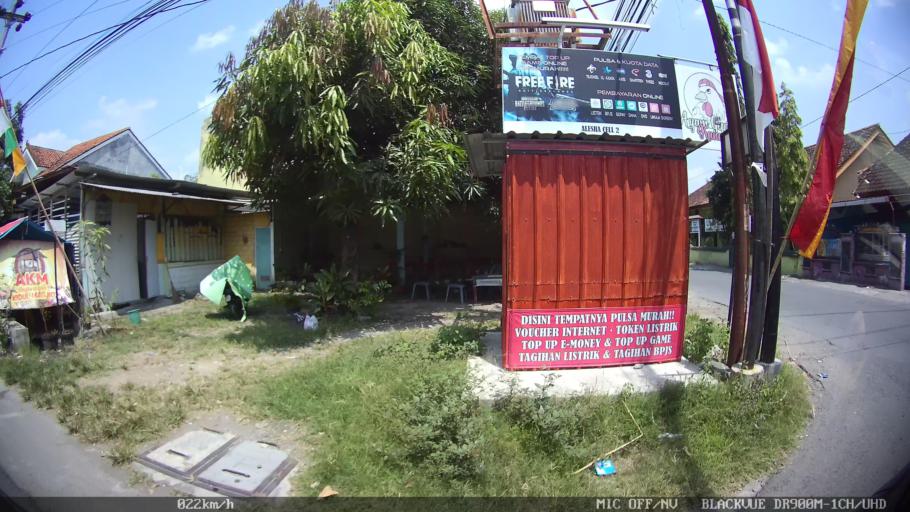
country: ID
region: Daerah Istimewa Yogyakarta
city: Yogyakarta
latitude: -7.8203
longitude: 110.4075
